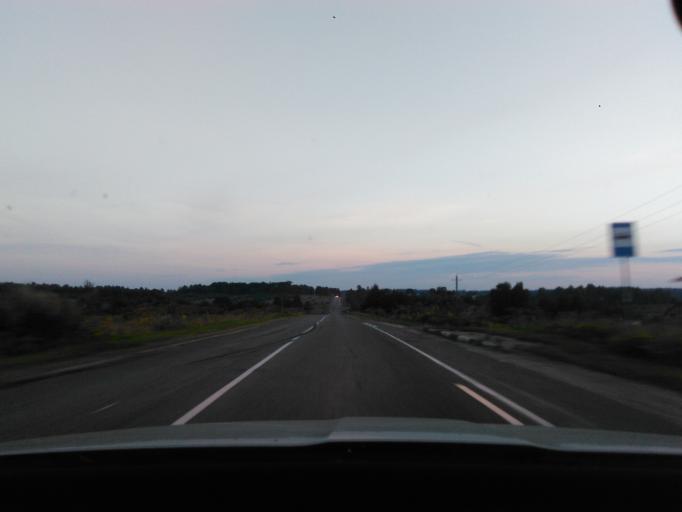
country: RU
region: Moskovskaya
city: Klin
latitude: 56.2215
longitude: 36.7367
